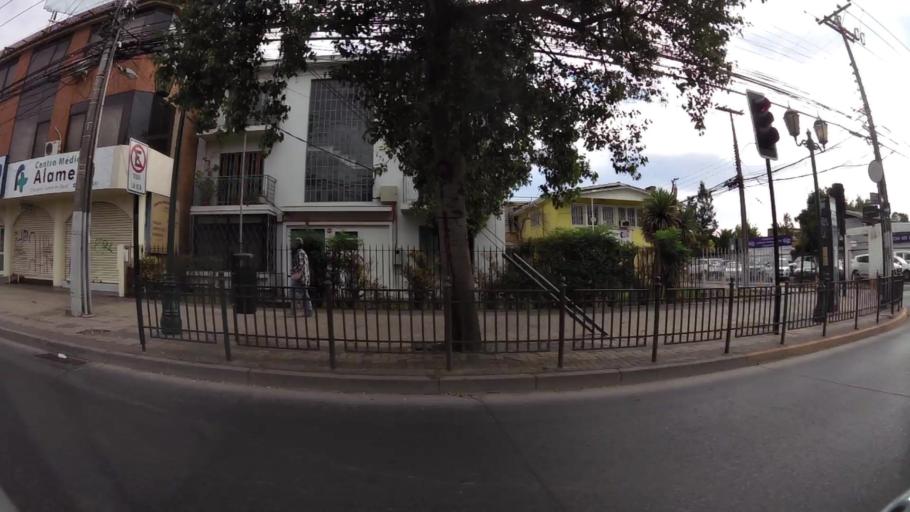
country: CL
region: O'Higgins
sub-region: Provincia de Cachapoal
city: Rancagua
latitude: -34.1658
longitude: -70.7395
